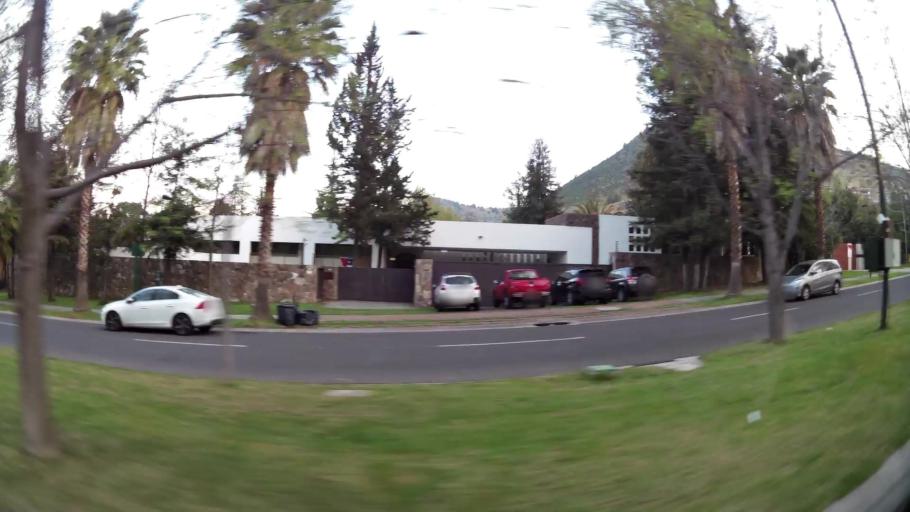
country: CL
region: Santiago Metropolitan
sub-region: Provincia de Chacabuco
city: Chicureo Abajo
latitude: -33.3402
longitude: -70.5585
